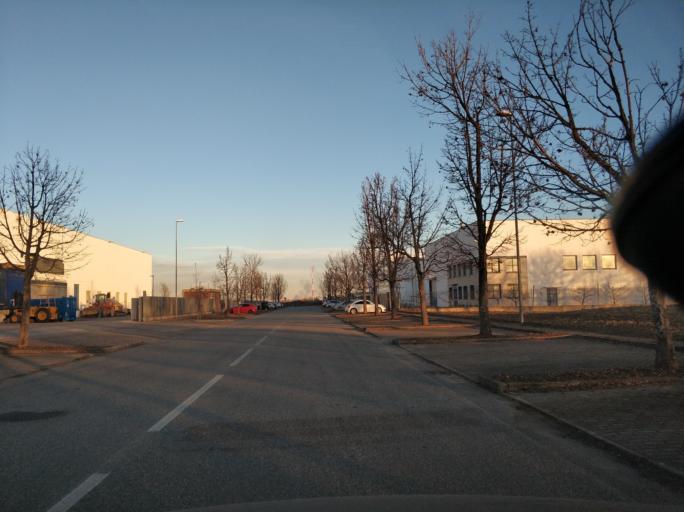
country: IT
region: Piedmont
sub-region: Provincia di Torino
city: San Maurizio
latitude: 45.2051
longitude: 7.6410
